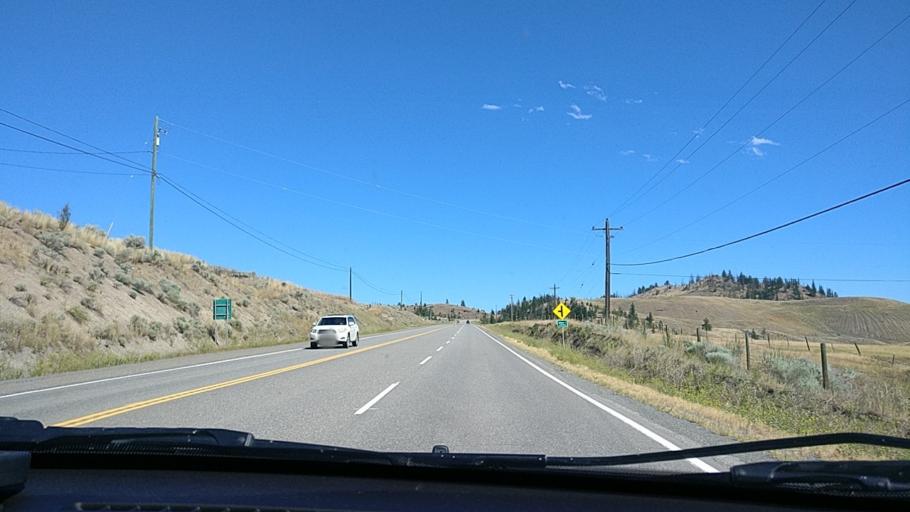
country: CA
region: British Columbia
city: Kamloops
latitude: 50.6625
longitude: -120.5515
